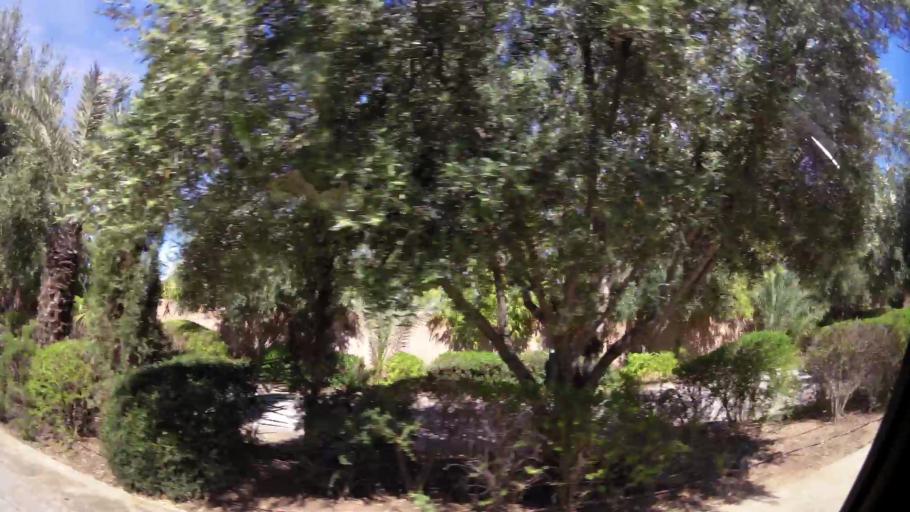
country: MA
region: Marrakech-Tensift-Al Haouz
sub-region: Marrakech
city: Marrakesh
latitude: 31.6035
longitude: -7.9534
